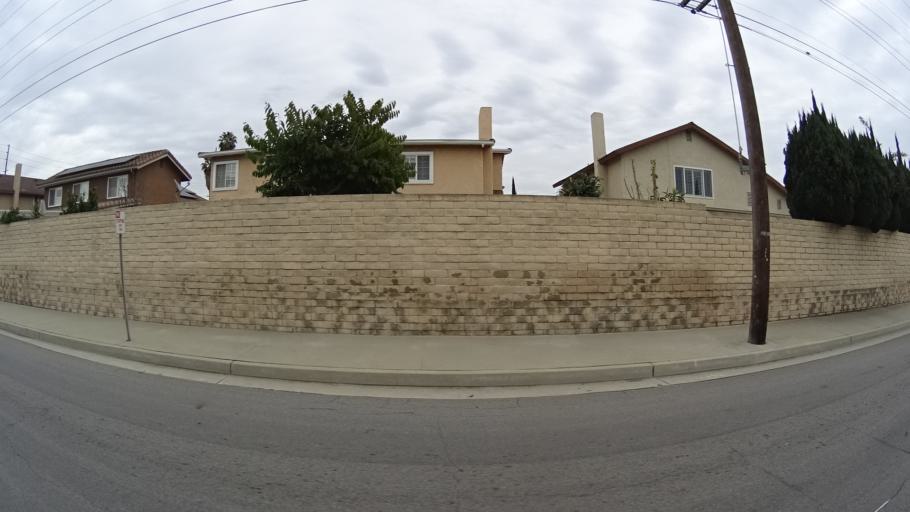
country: US
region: California
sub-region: Orange County
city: Midway City
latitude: 33.7365
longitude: -117.9807
